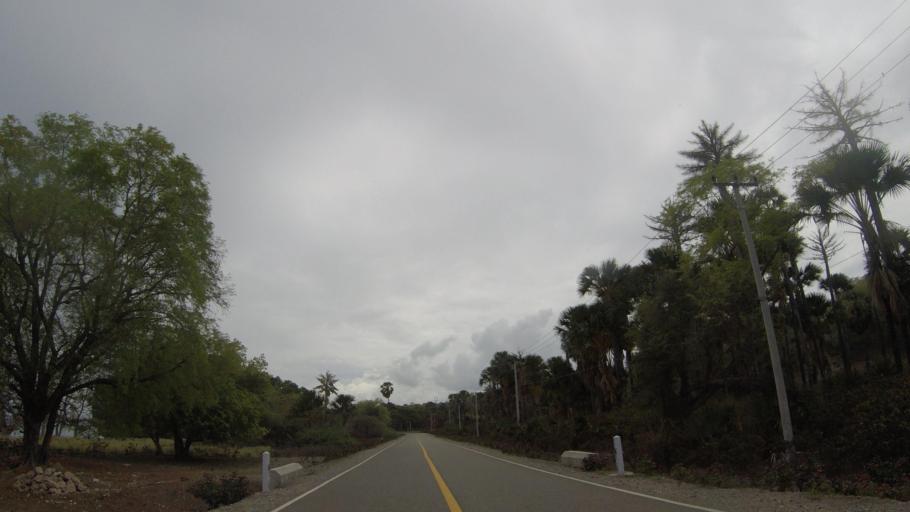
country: TL
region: Lautem
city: Lospalos
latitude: -8.4222
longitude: 126.7638
